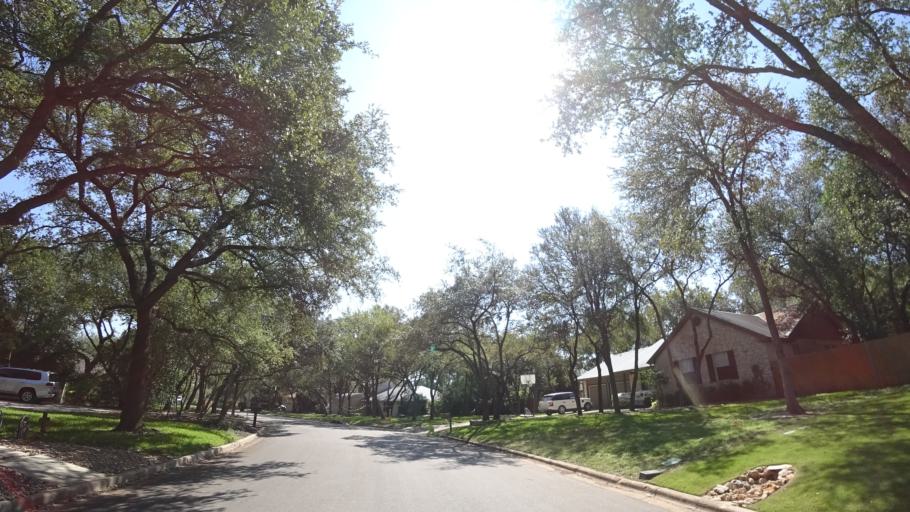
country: US
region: Texas
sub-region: Travis County
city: Rollingwood
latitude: 30.2775
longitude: -97.7895
